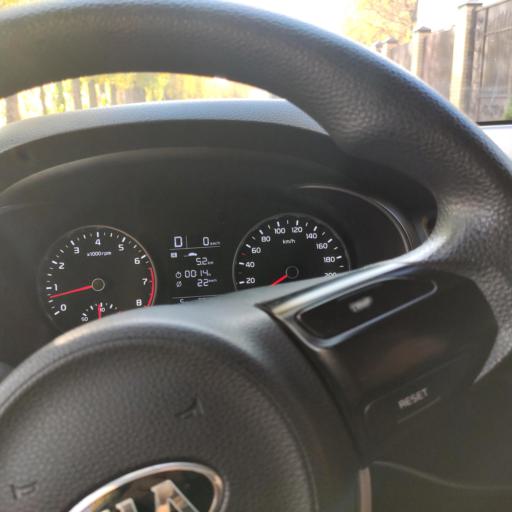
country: RU
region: Voronezj
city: Voronezh
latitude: 51.7035
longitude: 39.2375
